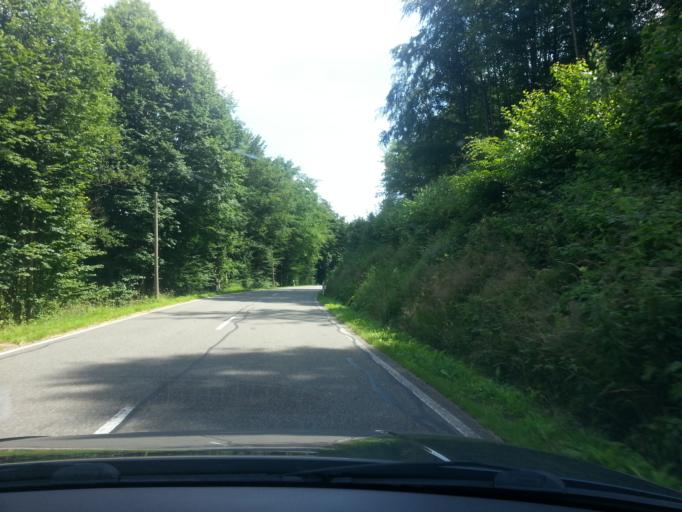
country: DE
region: Saarland
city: Spiesen-Elversberg
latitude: 49.3030
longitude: 7.1558
